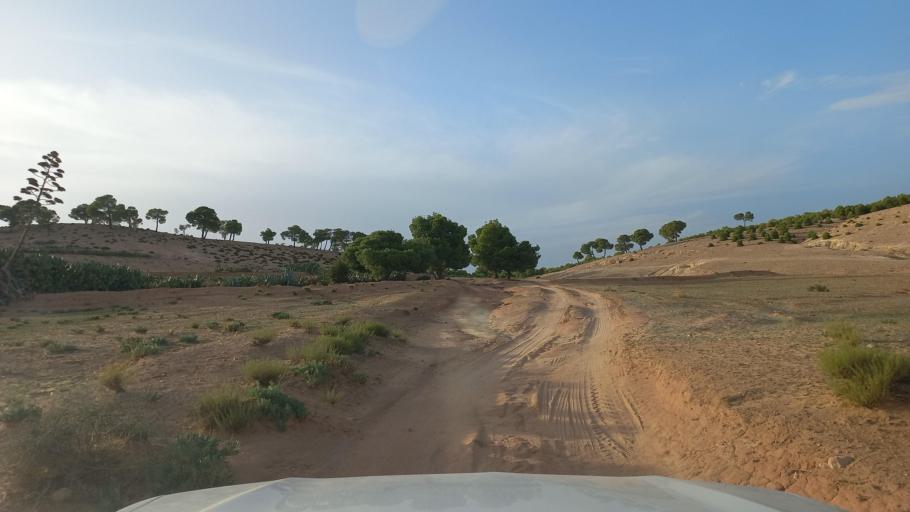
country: TN
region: Al Qasrayn
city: Sbiba
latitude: 35.4094
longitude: 8.8987
